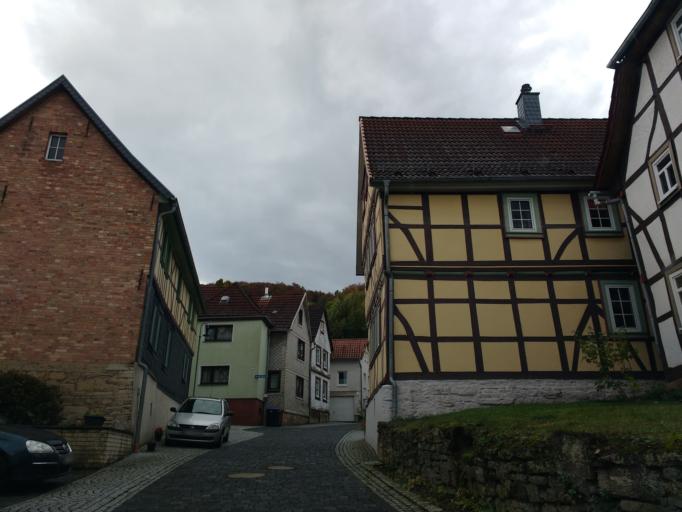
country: DE
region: Thuringia
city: Niederorschel
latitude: 51.3463
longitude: 10.4420
